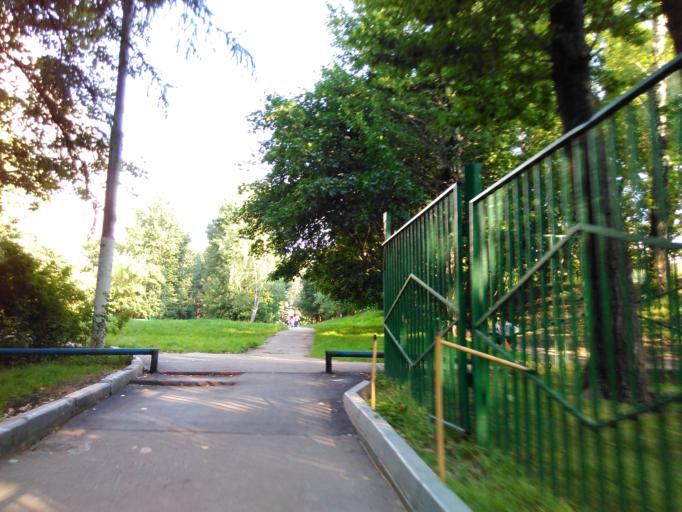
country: RU
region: Moskovskaya
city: Cheremushki
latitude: 55.6513
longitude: 37.5252
